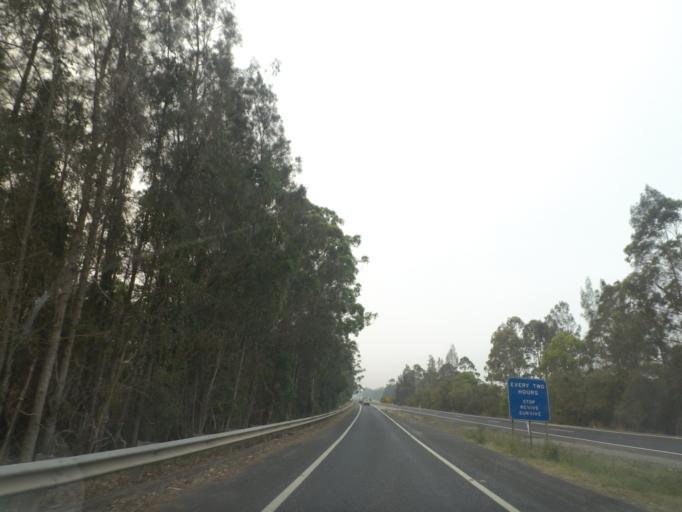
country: AU
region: New South Wales
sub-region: Port Macquarie-Hastings
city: Port Macquarie
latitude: -31.4603
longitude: 152.8205
